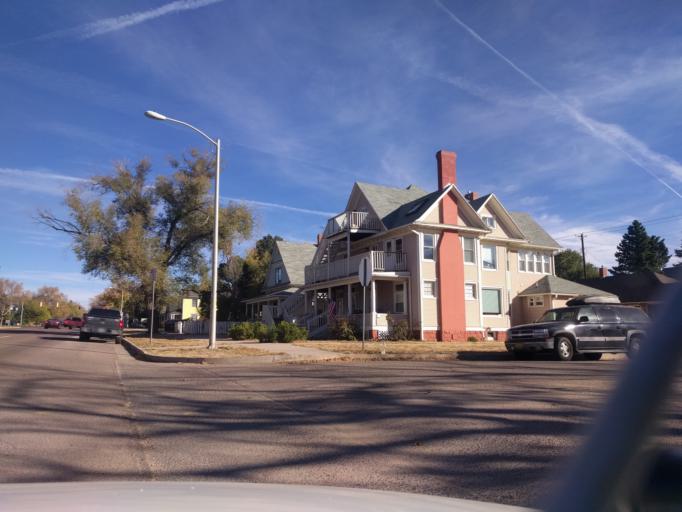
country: US
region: Colorado
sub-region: El Paso County
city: Colorado Springs
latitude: 38.8491
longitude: -104.8190
